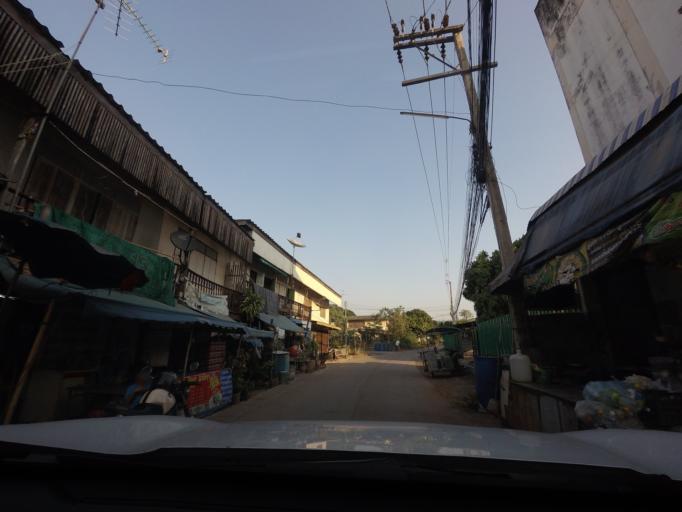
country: TH
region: Nakhon Ratchasima
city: Pak Chong
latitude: 14.6439
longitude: 101.3559
